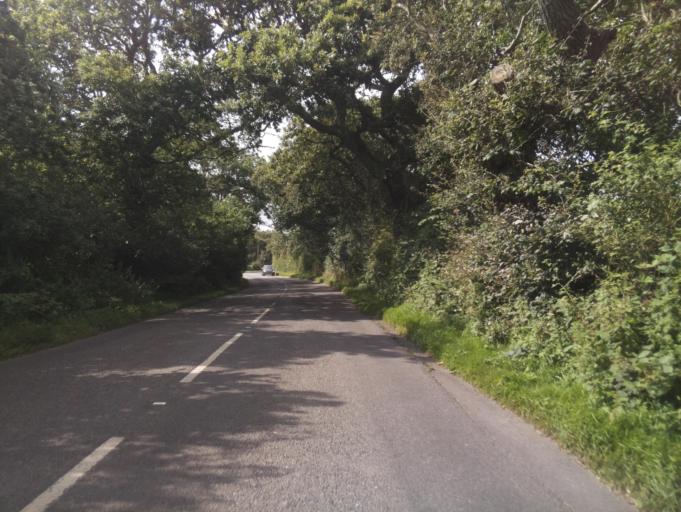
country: GB
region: England
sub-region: Hampshire
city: New Milton
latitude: 50.7399
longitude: -1.6423
